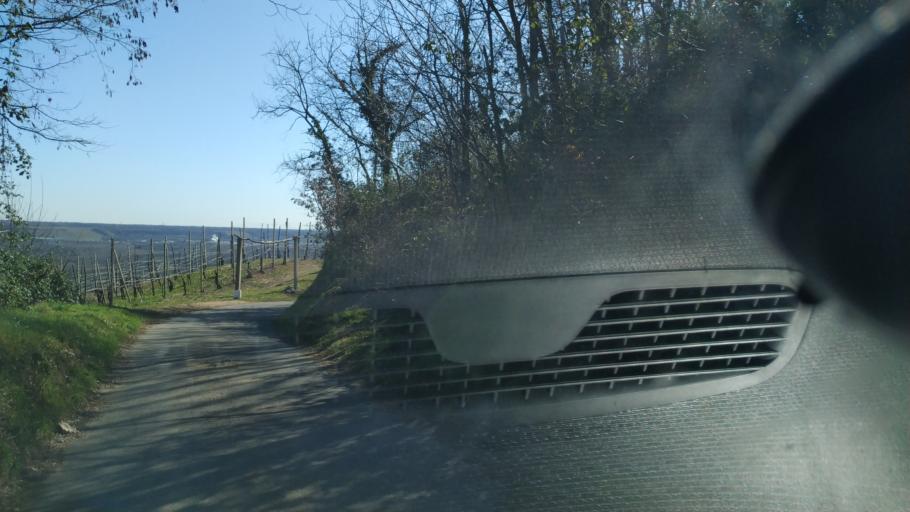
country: IT
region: Piedmont
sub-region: Provincia di Vercelli
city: Gattinara
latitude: 45.6237
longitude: 8.3643
